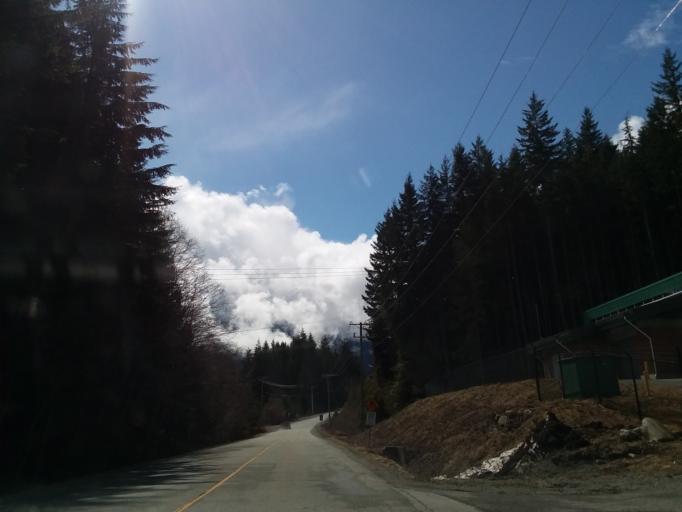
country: CA
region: British Columbia
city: Whistler
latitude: 50.1228
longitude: -122.9860
